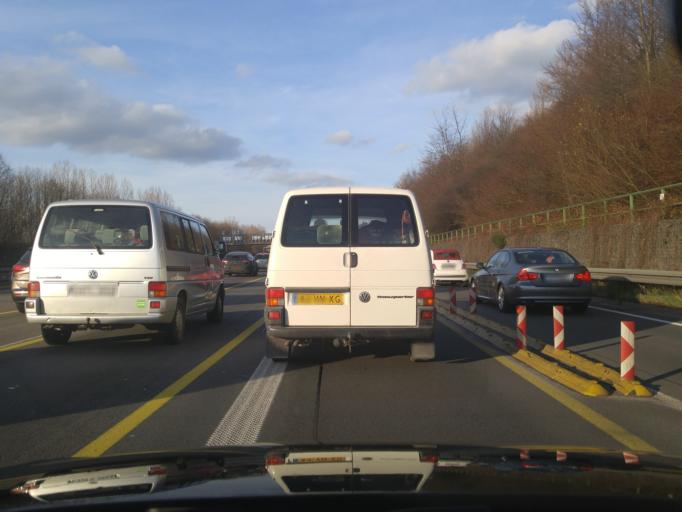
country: DE
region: North Rhine-Westphalia
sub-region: Regierungsbezirk Dusseldorf
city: Hilden
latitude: 51.2003
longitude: 6.9359
